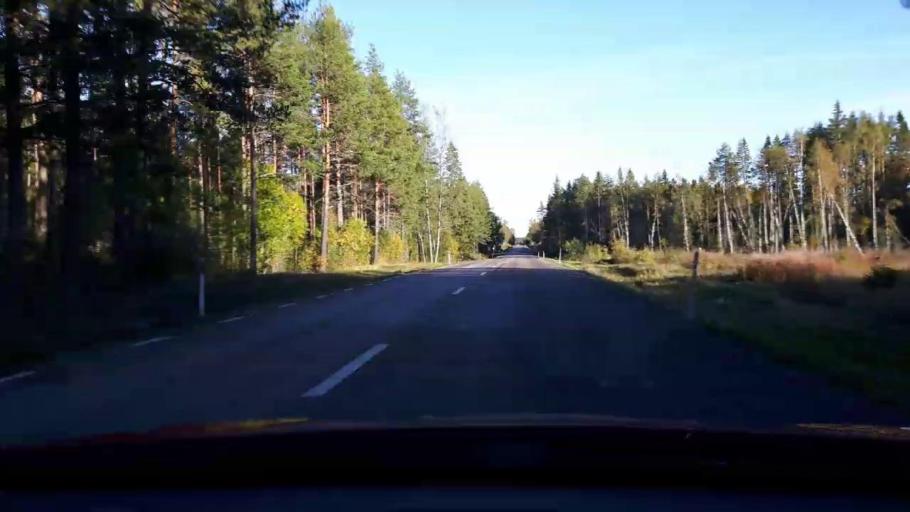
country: SE
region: Jaemtland
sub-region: OEstersunds Kommun
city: Brunflo
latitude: 63.0411
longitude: 14.8764
